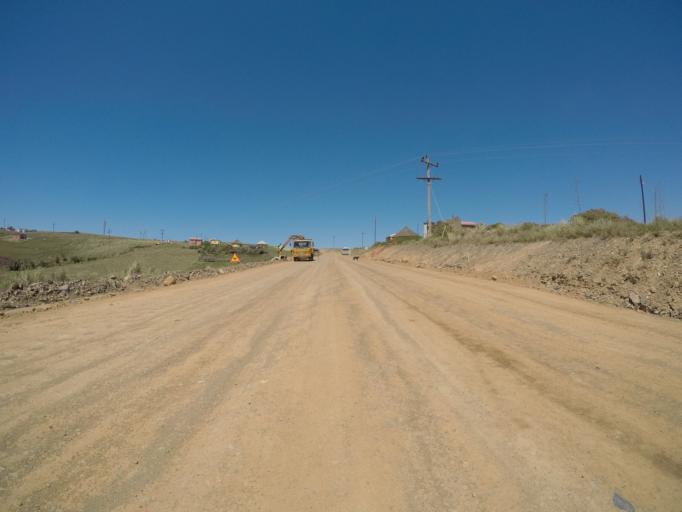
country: ZA
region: Eastern Cape
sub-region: OR Tambo District Municipality
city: Libode
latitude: -32.0213
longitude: 29.1150
